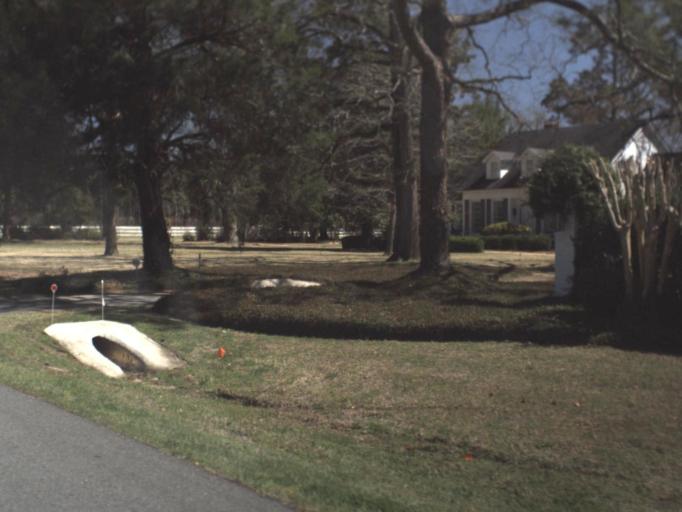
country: US
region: Florida
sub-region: Gadsden County
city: Quincy
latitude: 30.5244
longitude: -84.6043
